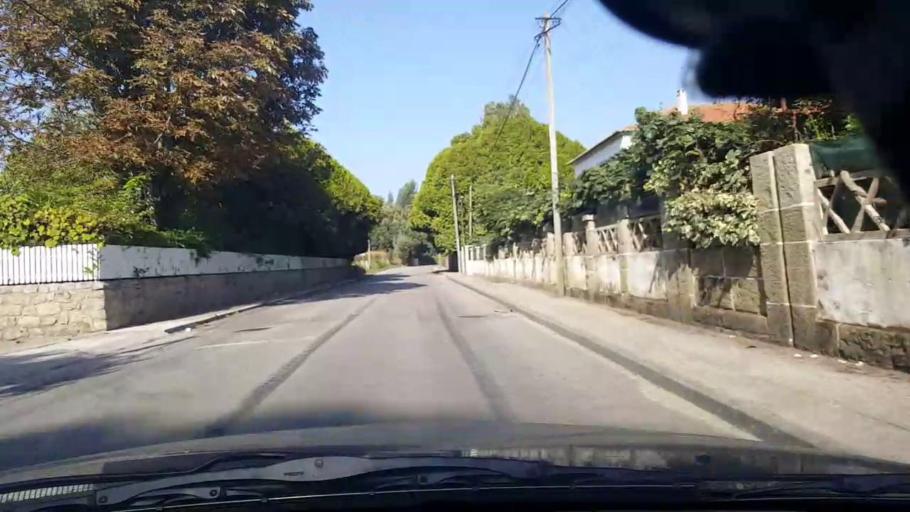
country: PT
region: Porto
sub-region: Maia
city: Gemunde
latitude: 41.2734
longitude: -8.6781
